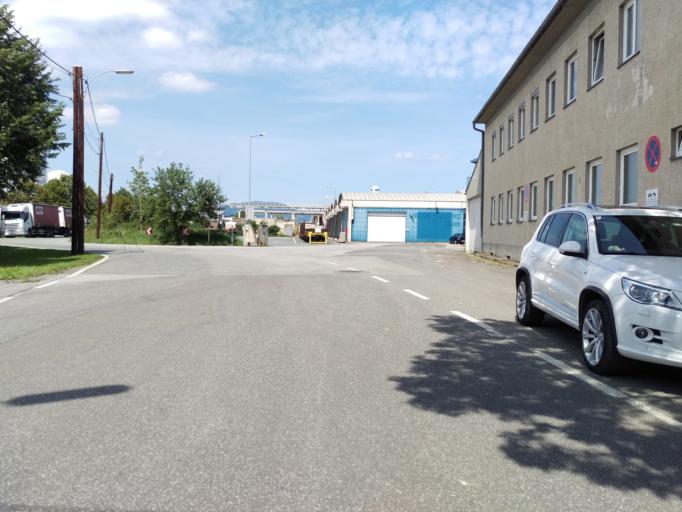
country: AT
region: Styria
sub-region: Graz Stadt
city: Wetzelsdorf
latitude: 47.0608
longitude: 15.4178
